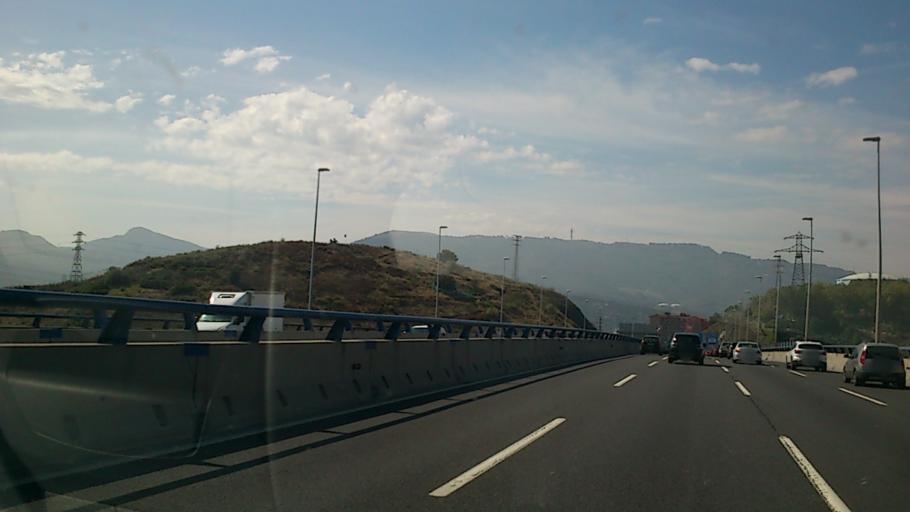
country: ES
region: Basque Country
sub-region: Bizkaia
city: Barakaldo
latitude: 43.2953
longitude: -2.9744
